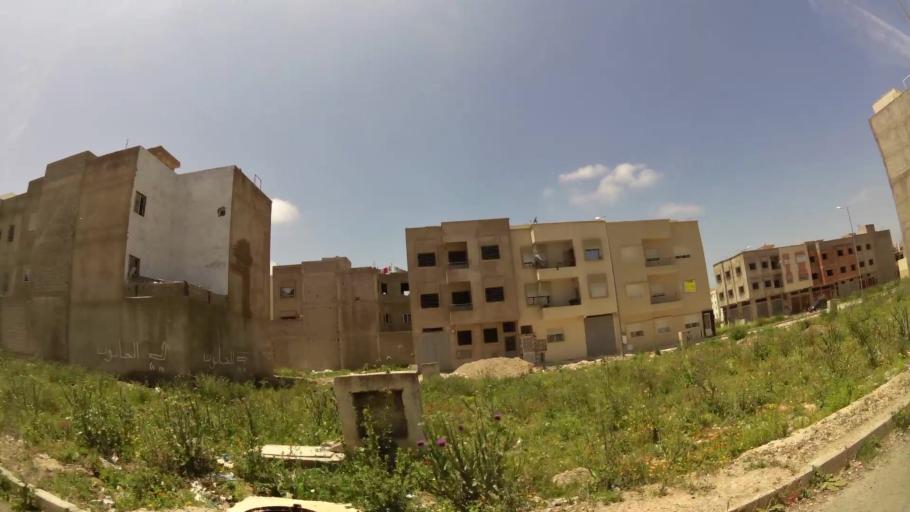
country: MA
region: Fes-Boulemane
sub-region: Fes
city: Fes
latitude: 34.0309
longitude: -5.0541
